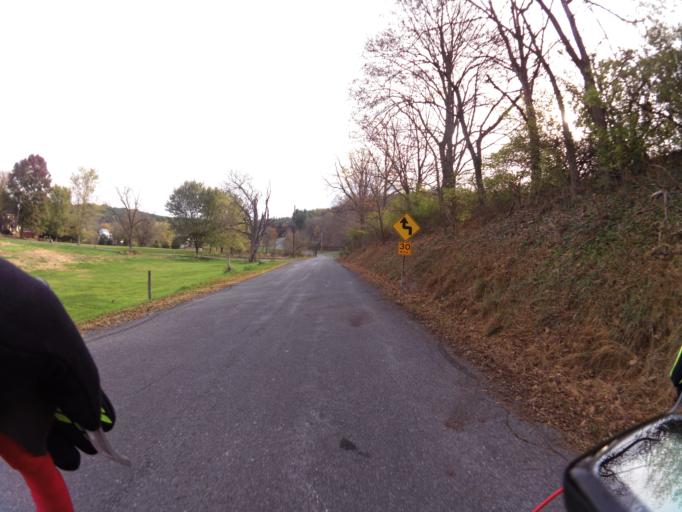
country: US
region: Pennsylvania
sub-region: Union County
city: New Columbia
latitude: 41.0285
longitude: -76.9245
